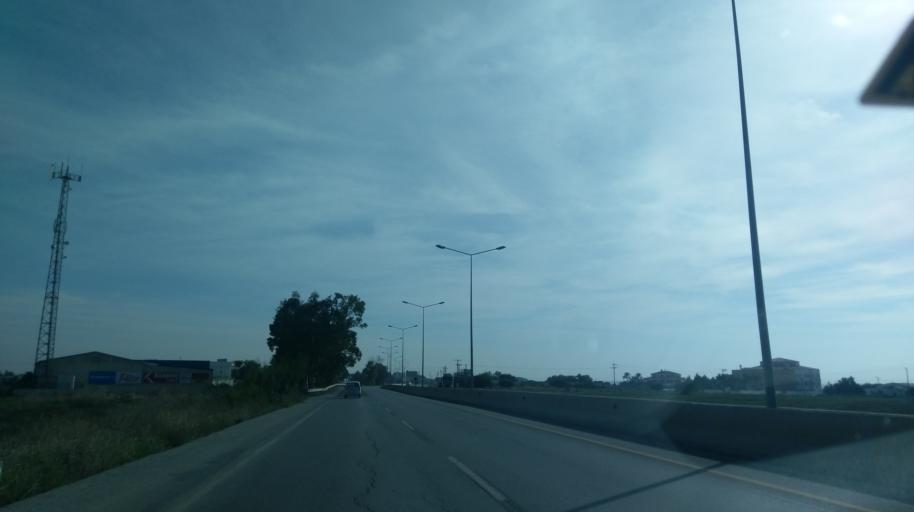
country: CY
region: Lefkosia
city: Geri
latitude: 35.2162
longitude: 33.5088
